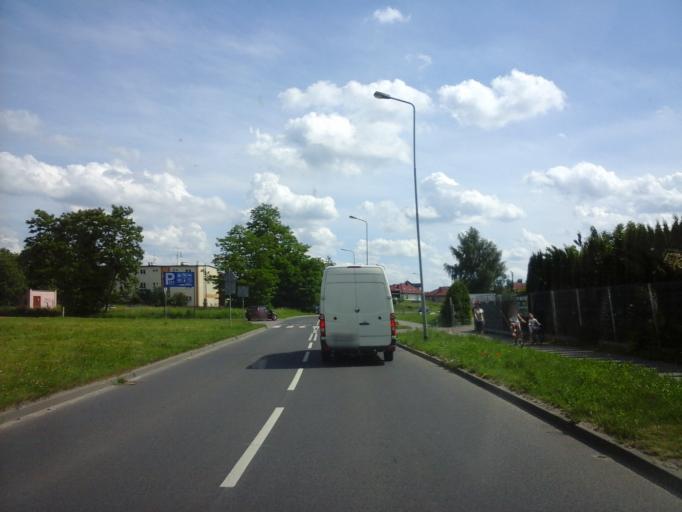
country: PL
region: West Pomeranian Voivodeship
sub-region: Powiat swidwinski
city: Swidwin
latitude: 53.7850
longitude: 15.7809
